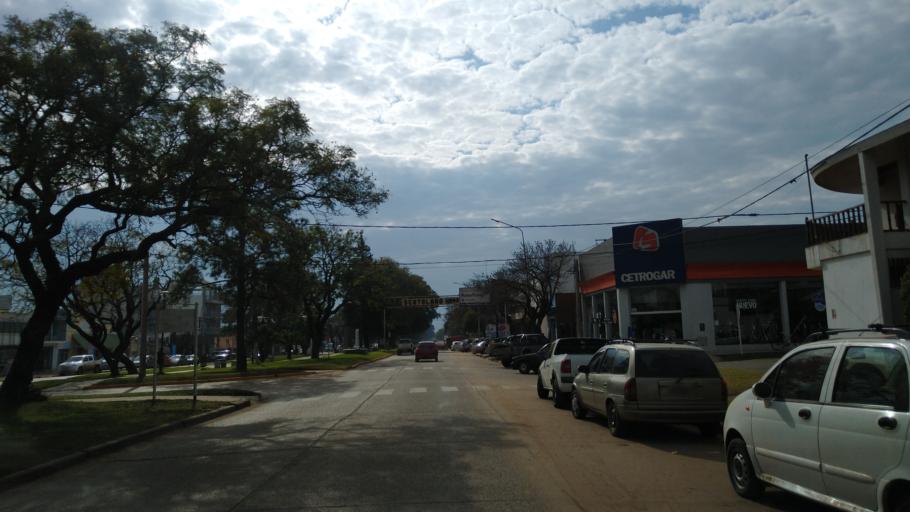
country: AR
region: Entre Rios
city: Chajari
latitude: -30.7580
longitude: -57.9877
